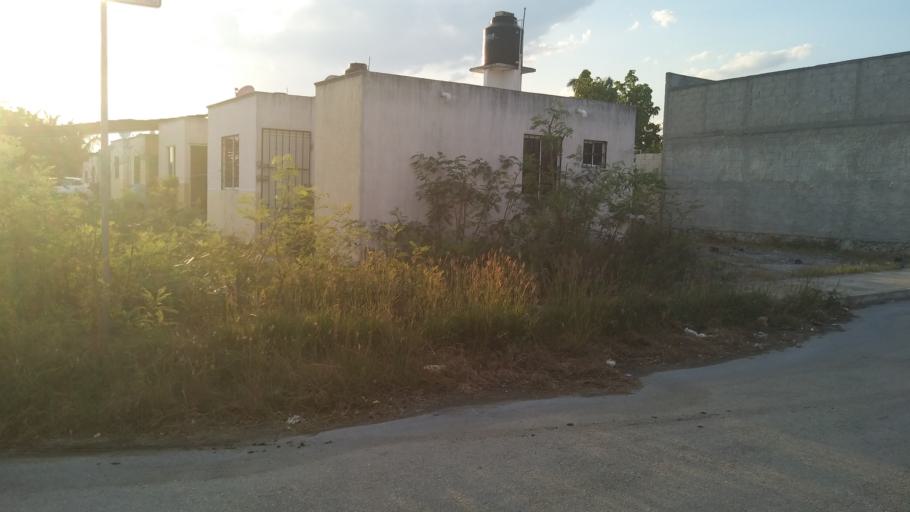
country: MX
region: Yucatan
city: Itzincab Palomeque
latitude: 20.9252
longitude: -89.6672
